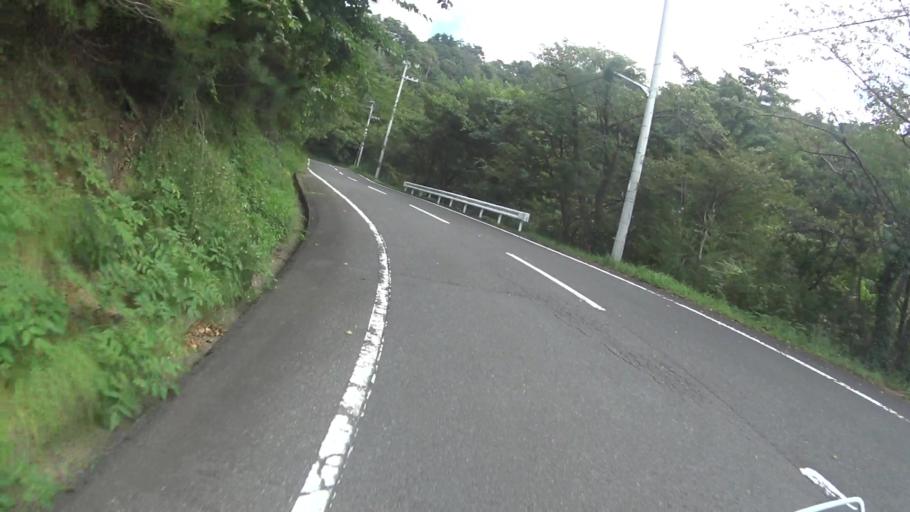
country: JP
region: Kyoto
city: Miyazu
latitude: 35.7336
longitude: 135.1756
